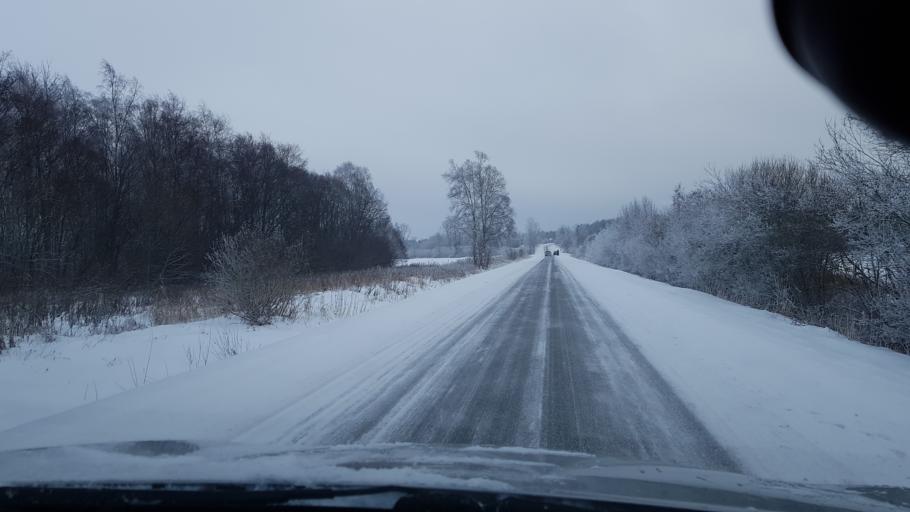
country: EE
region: Harju
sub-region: Keila linn
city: Keila
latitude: 59.3240
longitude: 24.4051
